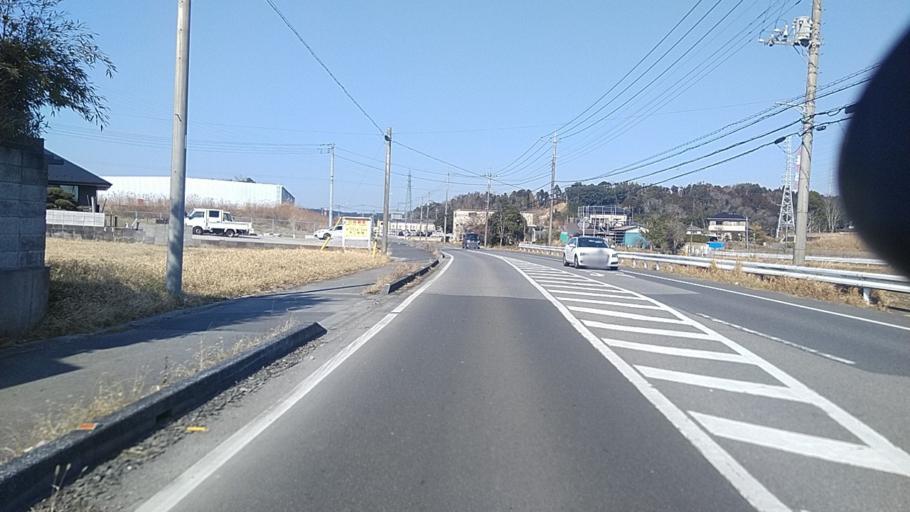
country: JP
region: Chiba
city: Mobara
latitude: 35.4684
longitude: 140.2824
